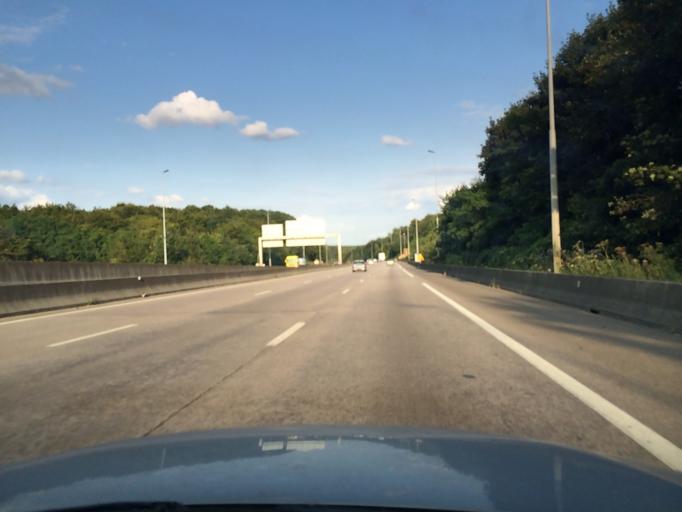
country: FR
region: Haute-Normandie
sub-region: Departement de la Seine-Maritime
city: Sahurs
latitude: 49.3394
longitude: 0.9473
